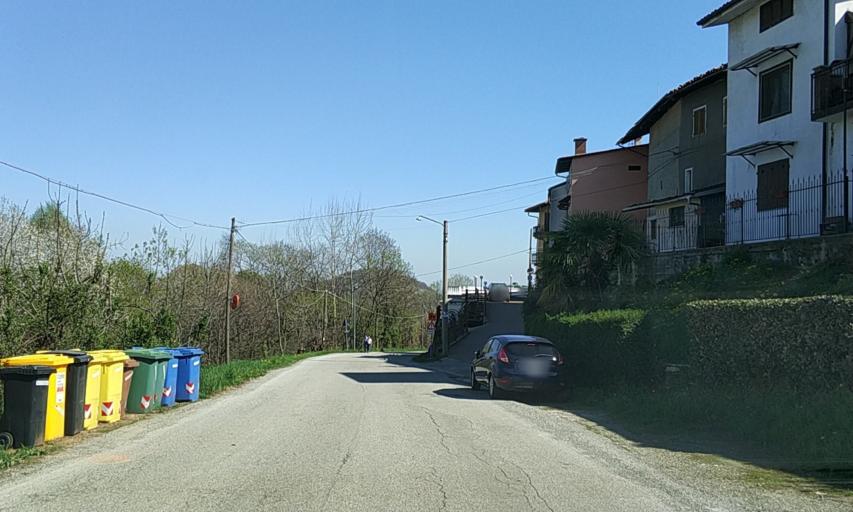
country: IT
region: Piedmont
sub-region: Provincia di Torino
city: Forno Canavese
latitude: 45.3397
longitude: 7.5881
